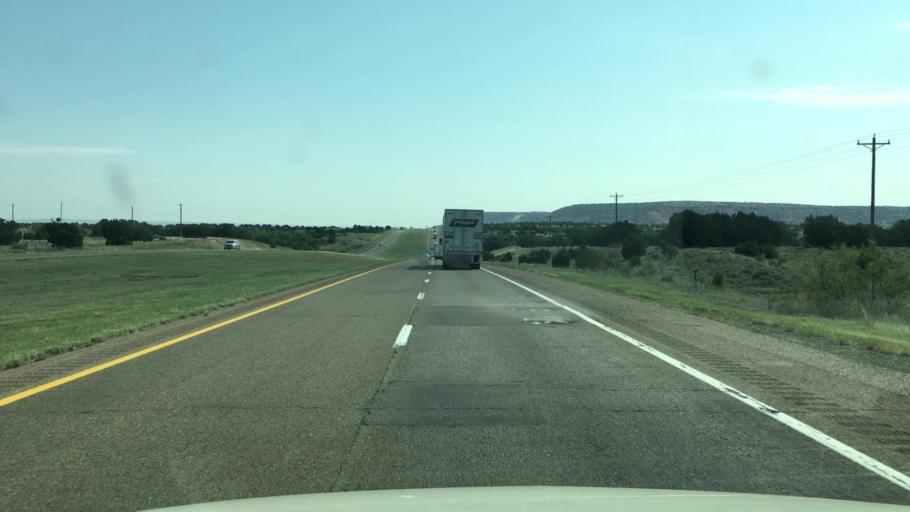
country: US
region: New Mexico
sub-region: Guadalupe County
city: Santa Rosa
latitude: 35.0172
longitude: -104.4408
